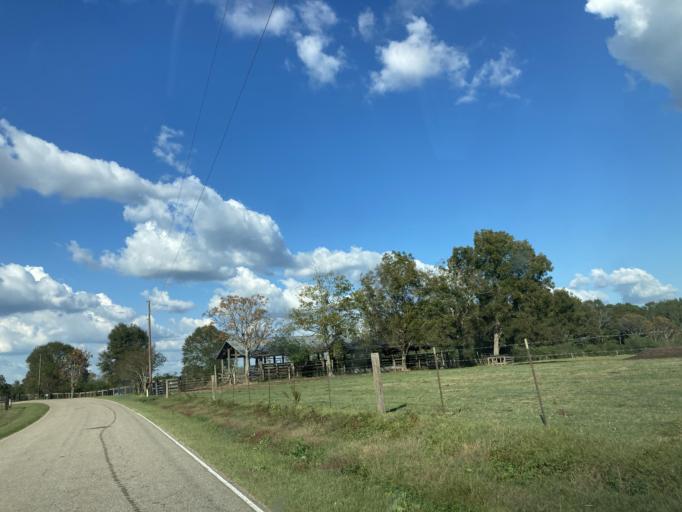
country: US
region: Mississippi
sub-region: Lamar County
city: Sumrall
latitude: 31.4179
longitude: -89.6244
